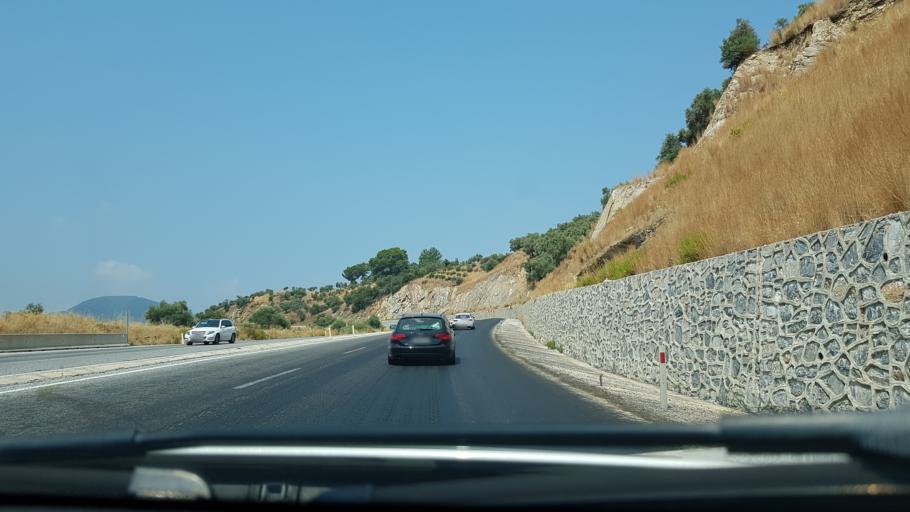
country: TR
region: Mugla
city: Selimiye
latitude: 37.4494
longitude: 27.5274
